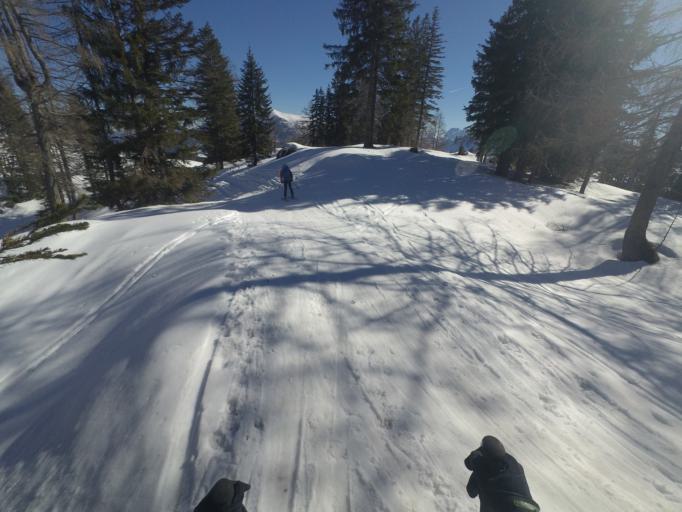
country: AT
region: Upper Austria
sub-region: Politischer Bezirk Gmunden
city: Sankt Wolfgang im Salzkammergut
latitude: 47.6591
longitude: 13.3886
